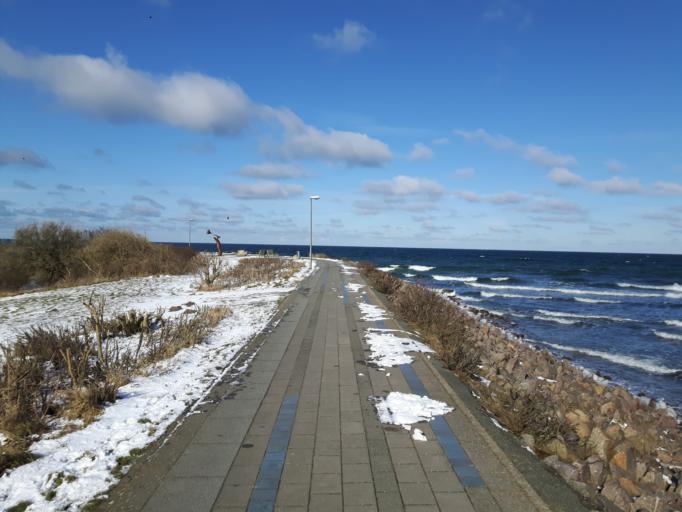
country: DE
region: Schleswig-Holstein
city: Heiligenhafen
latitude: 54.3840
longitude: 10.9522
